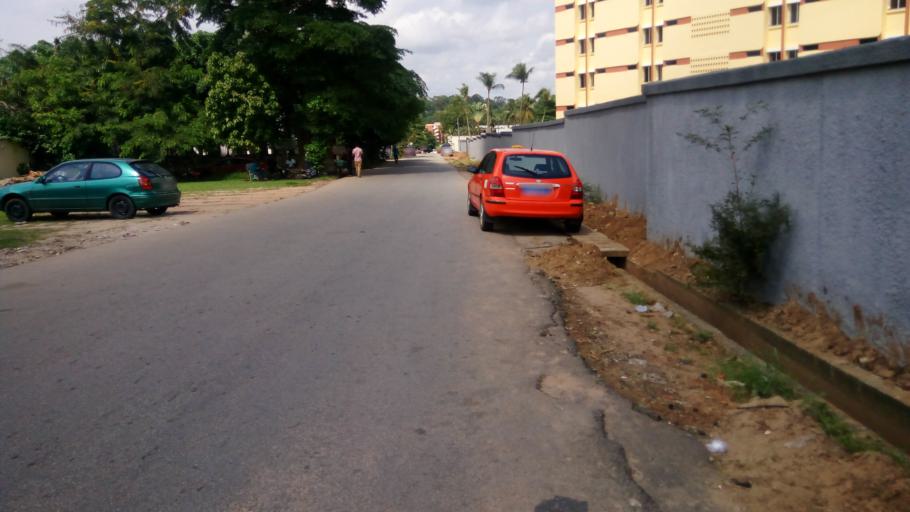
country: CI
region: Lagunes
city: Abidjan
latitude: 5.3388
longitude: -3.9958
